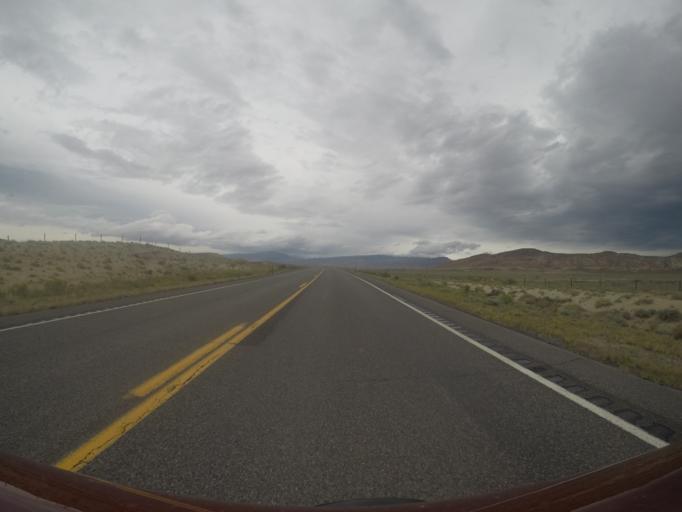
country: US
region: Wyoming
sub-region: Big Horn County
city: Lovell
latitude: 44.9148
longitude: -108.2926
